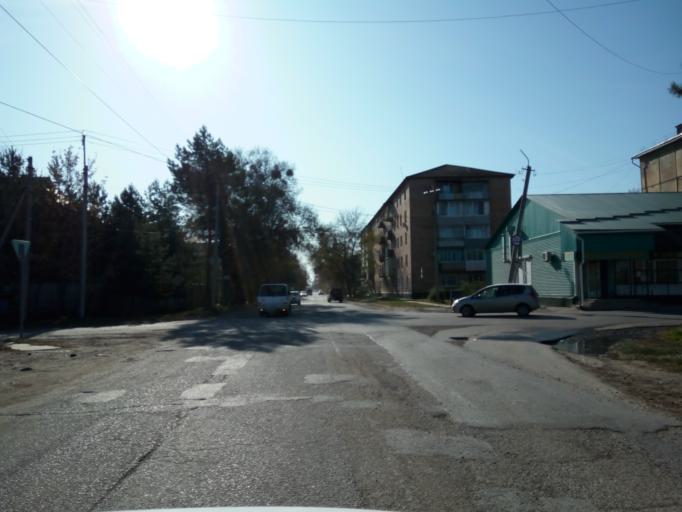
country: RU
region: Primorskiy
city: Dal'nerechensk
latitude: 45.9375
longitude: 133.7323
